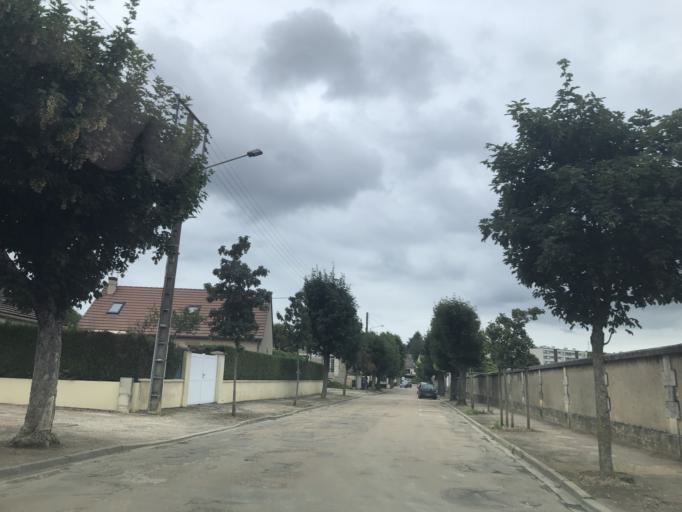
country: FR
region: Bourgogne
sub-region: Departement de l'Yonne
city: Auxerre
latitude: 47.8065
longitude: 3.5678
